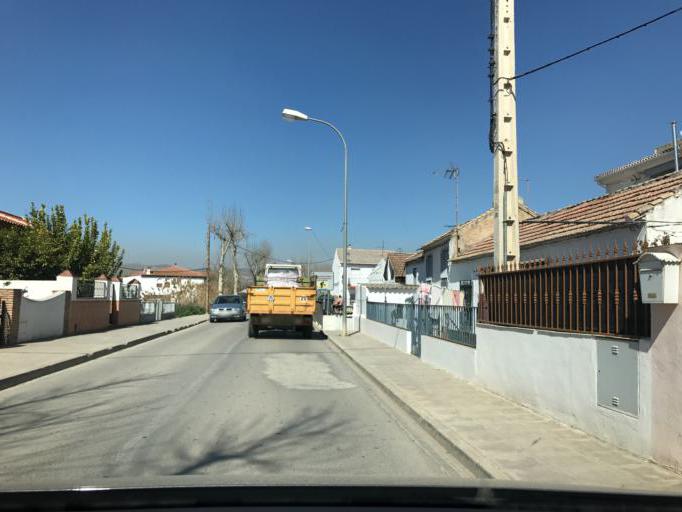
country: ES
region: Andalusia
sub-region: Provincia de Granada
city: Fuente Vaqueros
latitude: 37.2259
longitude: -3.7870
